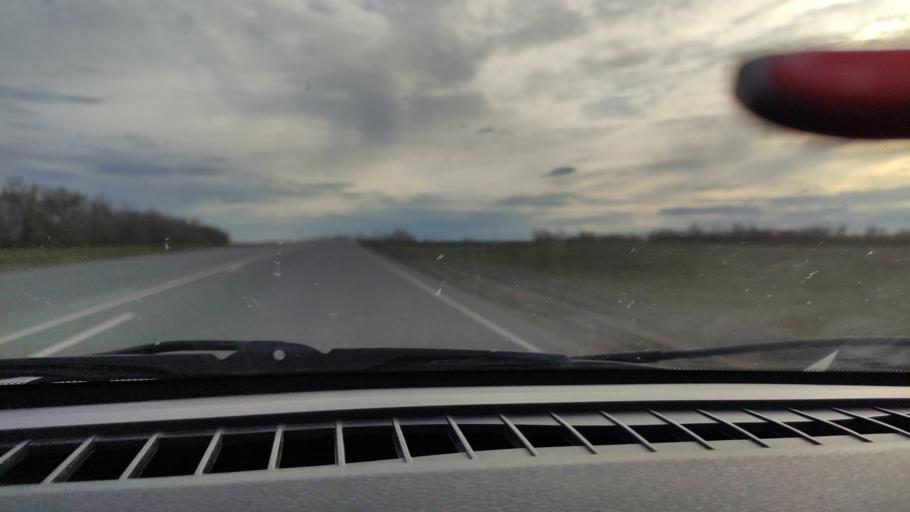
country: RU
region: Orenburg
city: Tatarskaya Kargala
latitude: 52.0203
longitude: 55.2140
